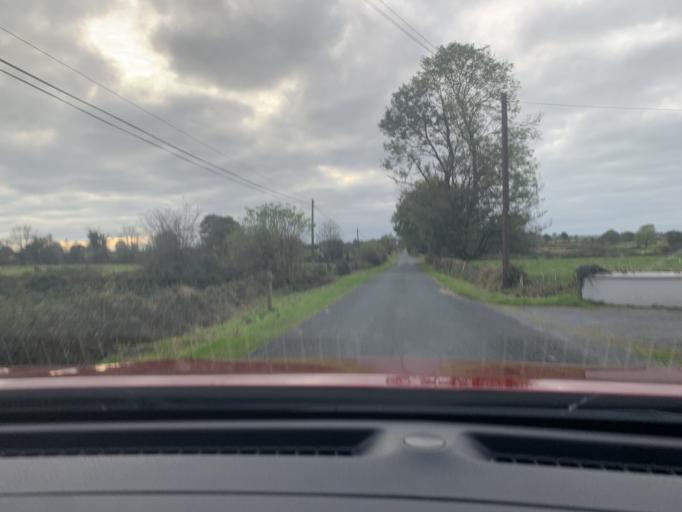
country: IE
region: Connaught
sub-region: Sligo
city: Tobercurry
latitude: 54.0289
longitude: -8.6784
